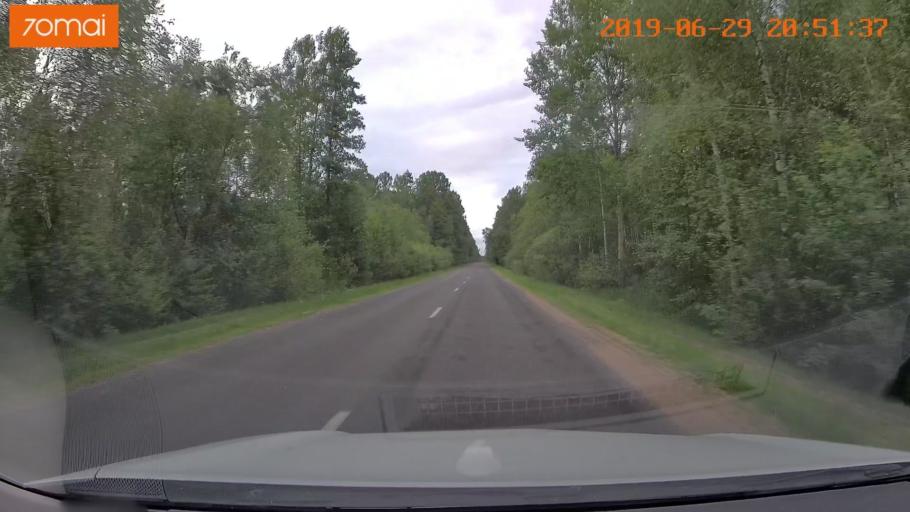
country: BY
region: Brest
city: Hantsavichy
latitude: 52.6901
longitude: 26.3518
